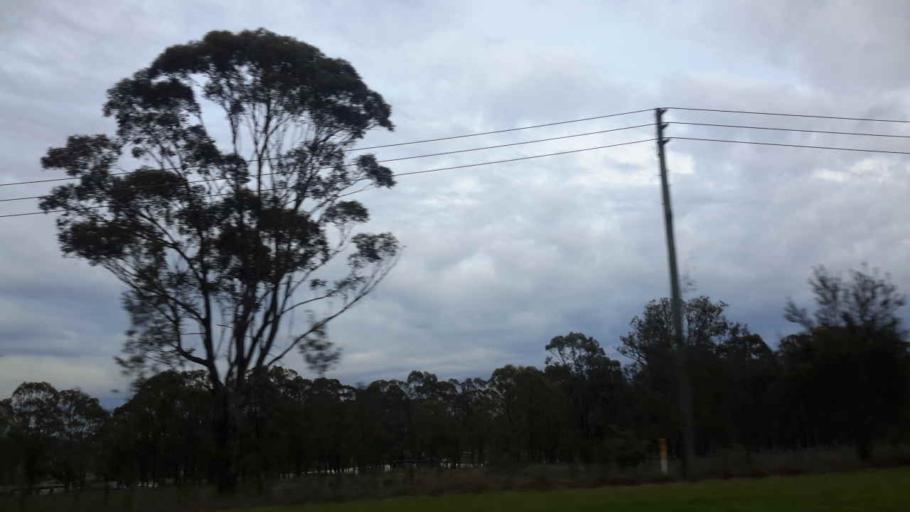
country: AU
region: New South Wales
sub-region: Camden
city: Camden South
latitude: -34.1089
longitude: 150.6973
